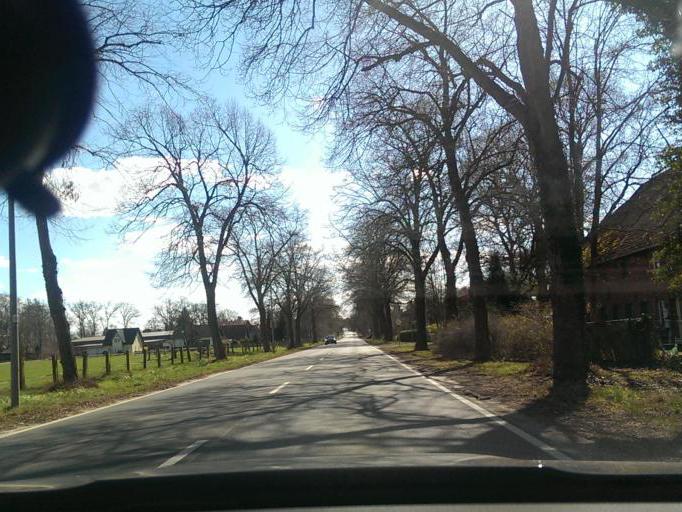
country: DE
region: Lower Saxony
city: Elze
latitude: 52.5675
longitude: 9.7260
